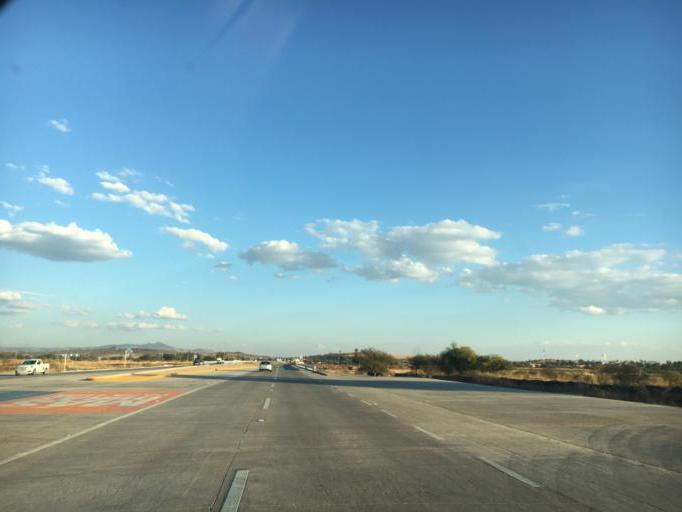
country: MX
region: Guanajuato
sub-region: Leon
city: Ladrilleras del Refugio
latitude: 21.0824
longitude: -101.5533
